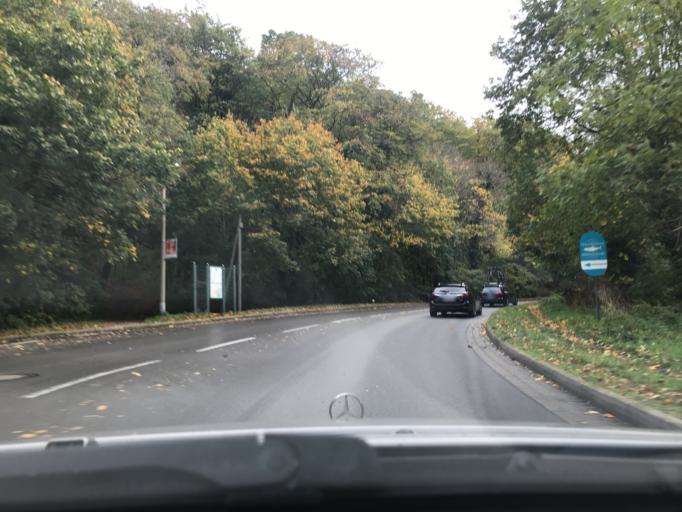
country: DE
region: Mecklenburg-Vorpommern
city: Seebad Heringsdorf
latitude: 53.9567
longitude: 14.1578
